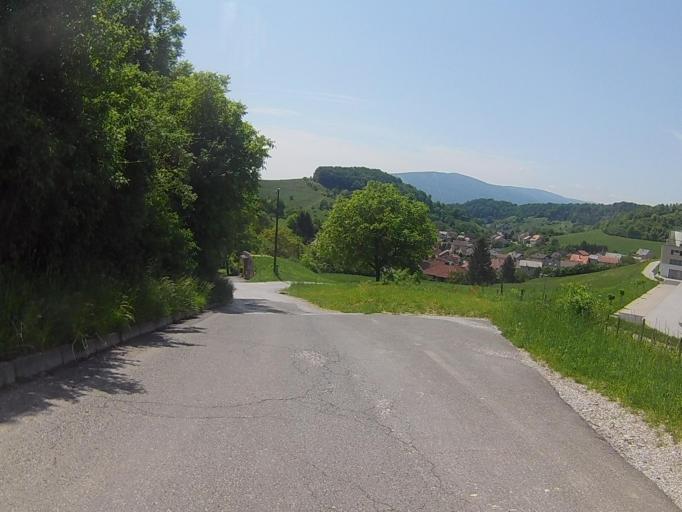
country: SI
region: Pesnica
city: Pesnica pri Mariboru
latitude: 46.5791
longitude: 15.6715
